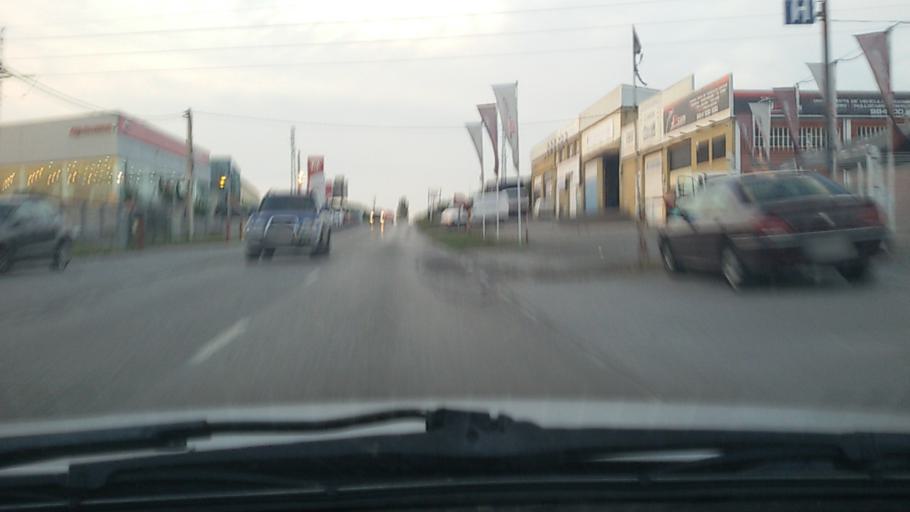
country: ES
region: Asturias
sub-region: Province of Asturias
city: Lugones
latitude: 43.3847
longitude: -5.7842
